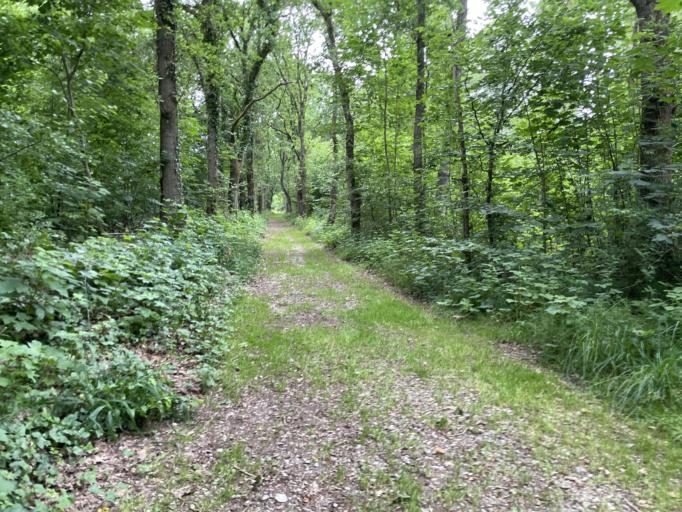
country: DK
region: South Denmark
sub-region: Varde Kommune
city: Olgod
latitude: 55.7058
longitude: 8.6433
